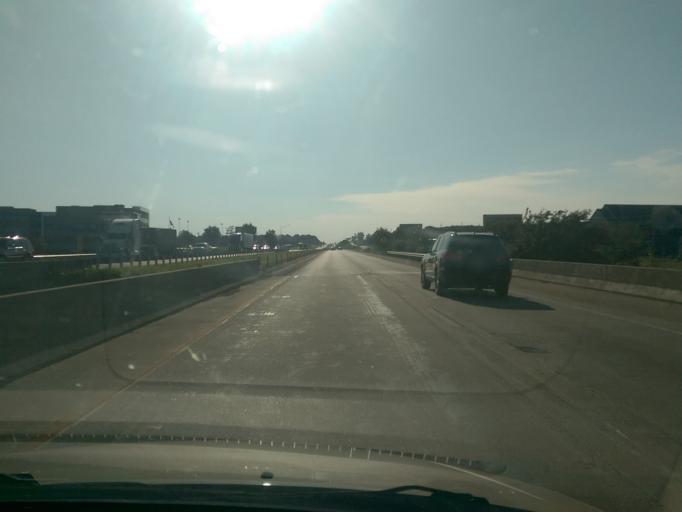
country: US
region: Missouri
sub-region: Jackson County
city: Grain Valley
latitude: 39.0214
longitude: -94.1977
